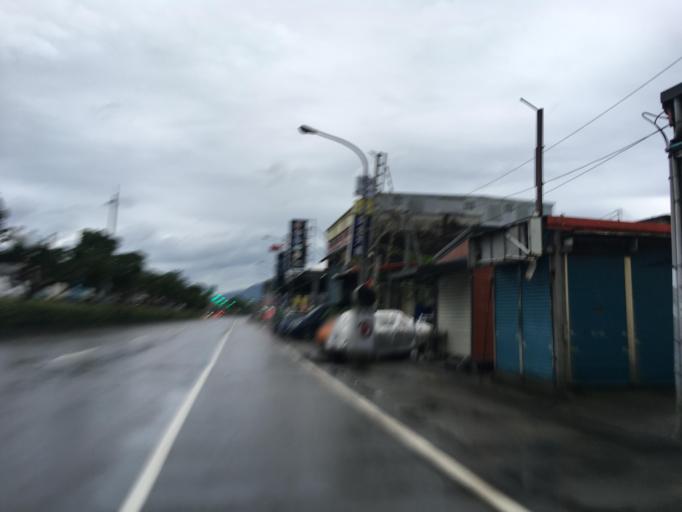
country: TW
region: Taiwan
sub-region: Yilan
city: Yilan
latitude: 24.6555
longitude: 121.7797
